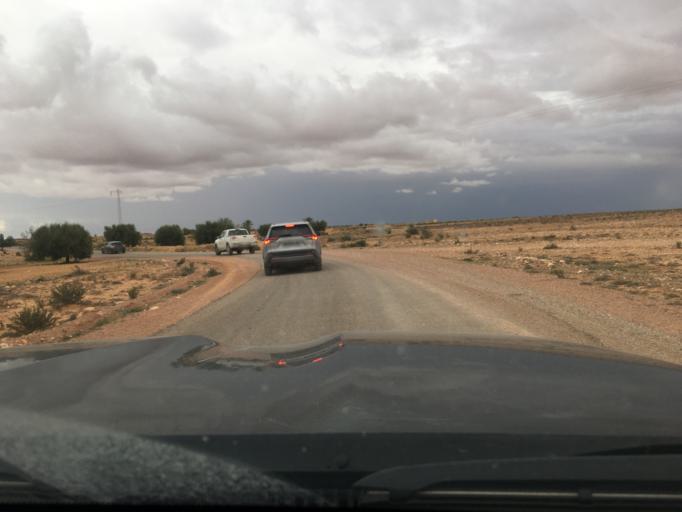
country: TN
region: Madanin
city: Medenine
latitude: 33.2876
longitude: 10.6037
